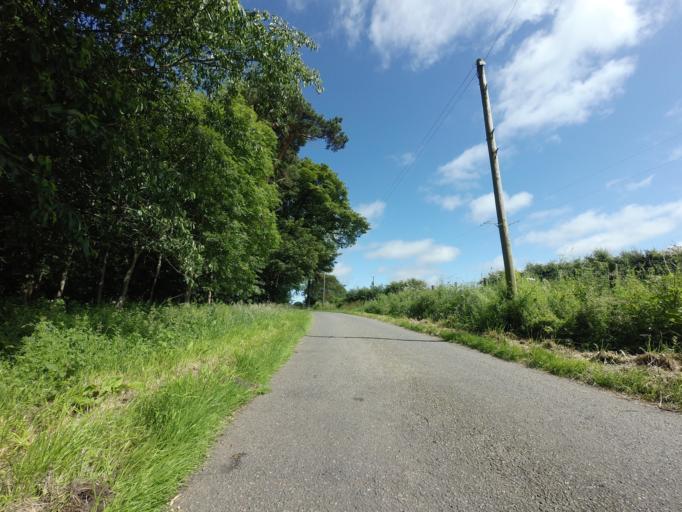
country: GB
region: Scotland
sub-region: Aberdeenshire
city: Turriff
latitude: 57.5853
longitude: -2.5042
